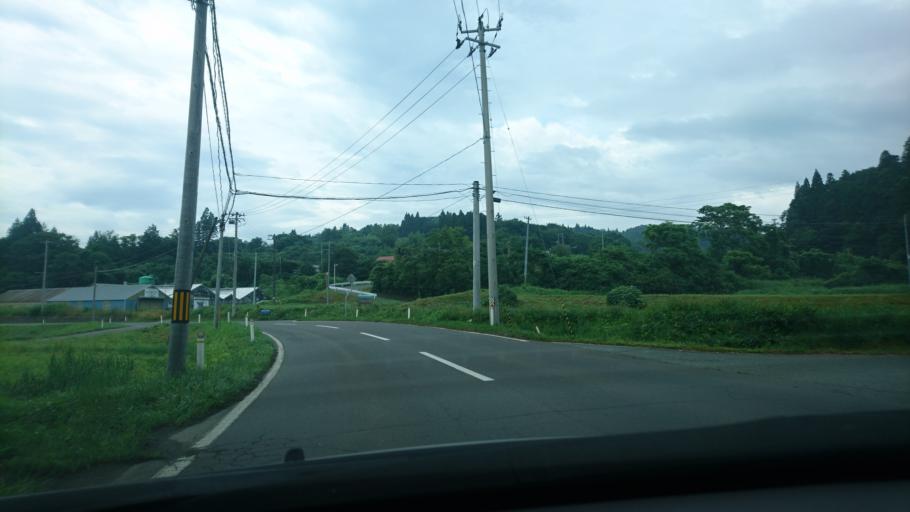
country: JP
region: Iwate
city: Ichinoseki
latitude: 38.9286
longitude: 141.4198
